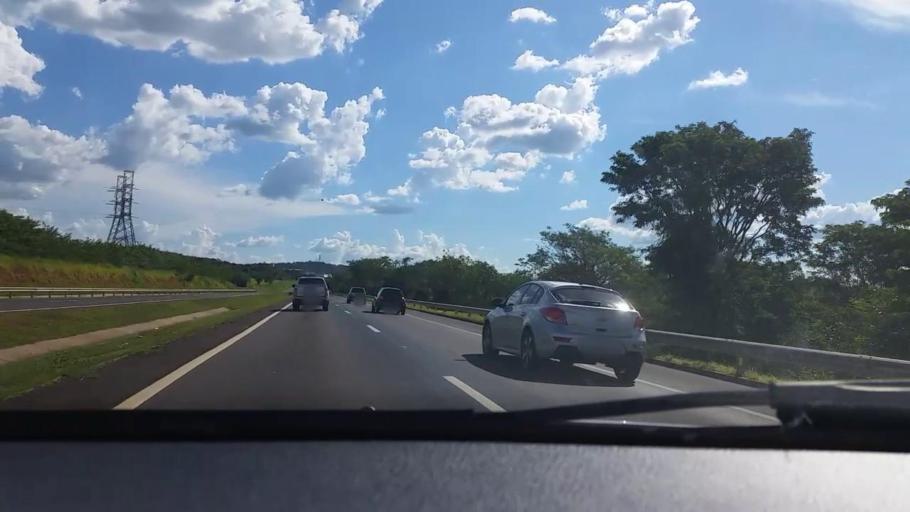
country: BR
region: Sao Paulo
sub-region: Bauru
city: Bauru
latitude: -22.4100
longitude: -49.1014
